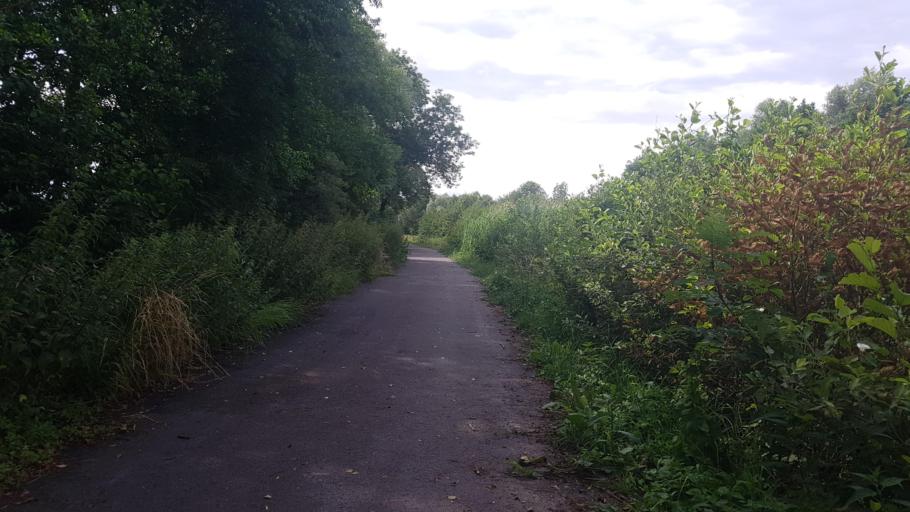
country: FR
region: Lorraine
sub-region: Departement de la Moselle
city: Dieuze
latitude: 48.6850
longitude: 6.7775
